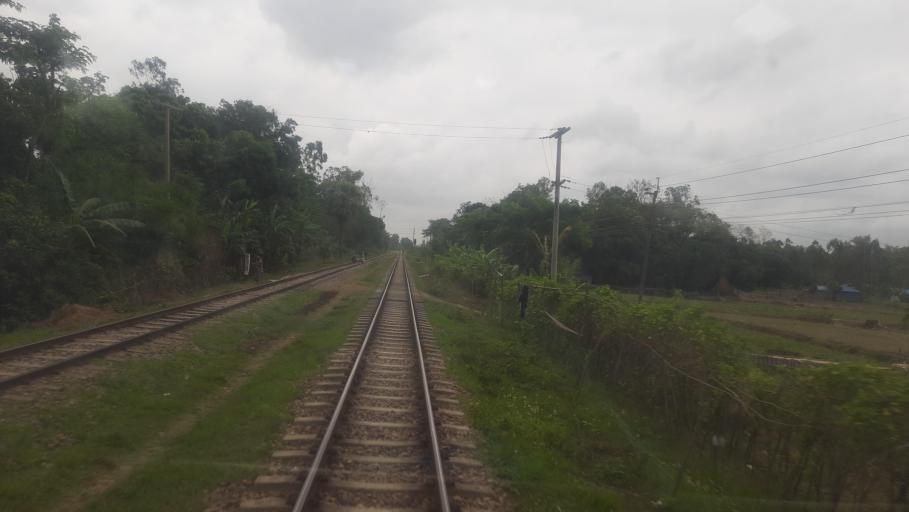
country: BD
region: Chittagong
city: Fatikchari
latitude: 22.7632
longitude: 91.5937
